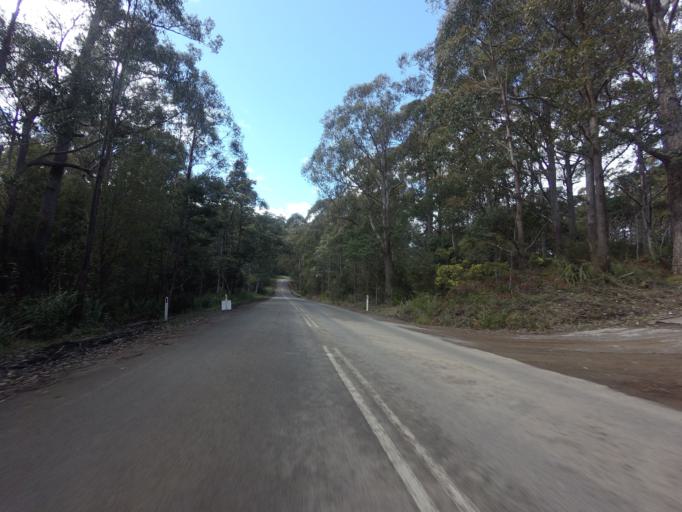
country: AU
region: Tasmania
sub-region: Huon Valley
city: Geeveston
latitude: -43.4135
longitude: 146.9170
